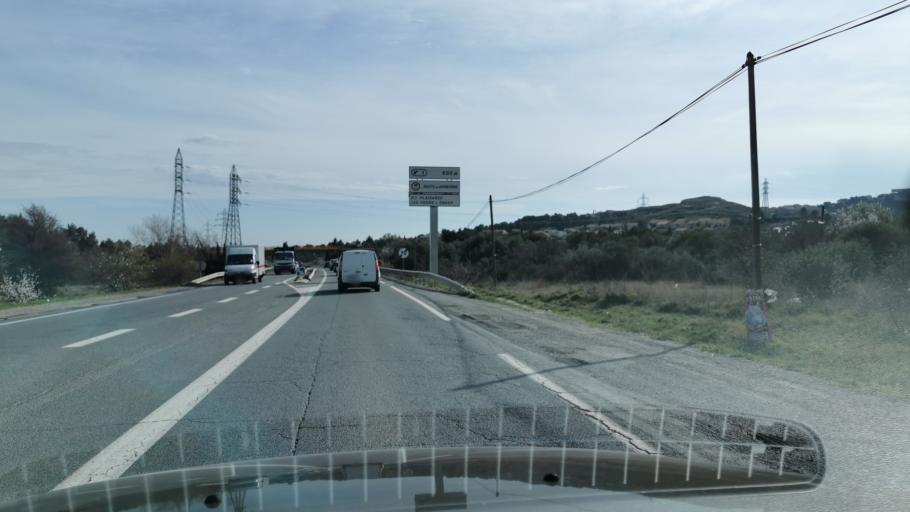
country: FR
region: Languedoc-Roussillon
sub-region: Departement de l'Aude
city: Narbonne
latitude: 43.1736
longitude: 2.9753
